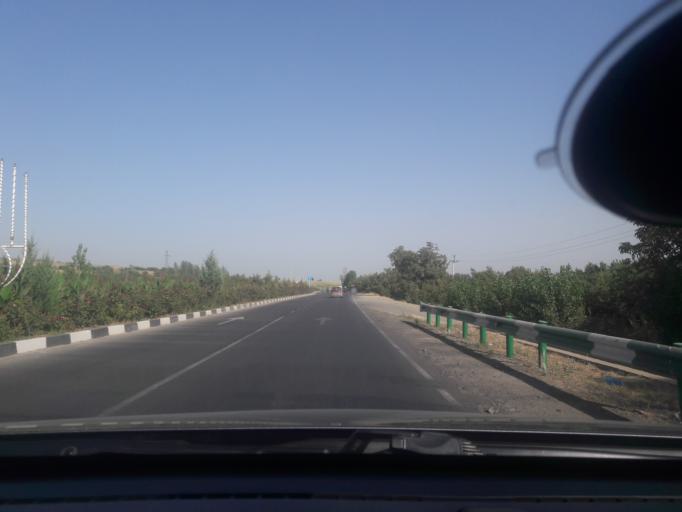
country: TJ
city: Shahrinav
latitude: 38.5740
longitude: 68.3616
